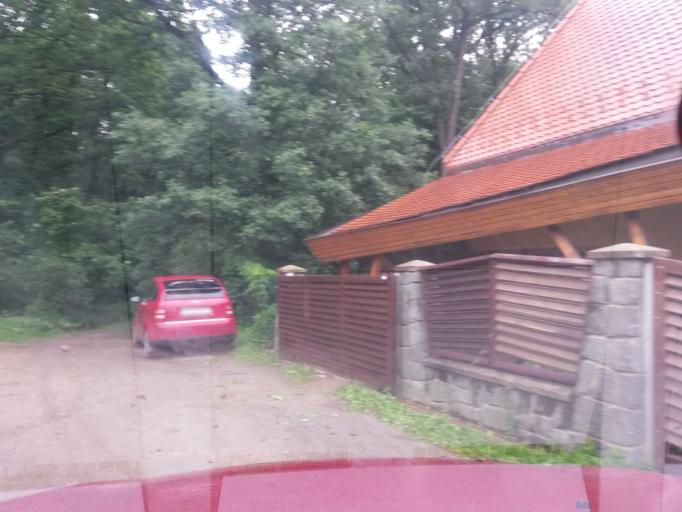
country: SK
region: Kosicky
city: Kosice
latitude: 48.7086
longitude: 21.1889
